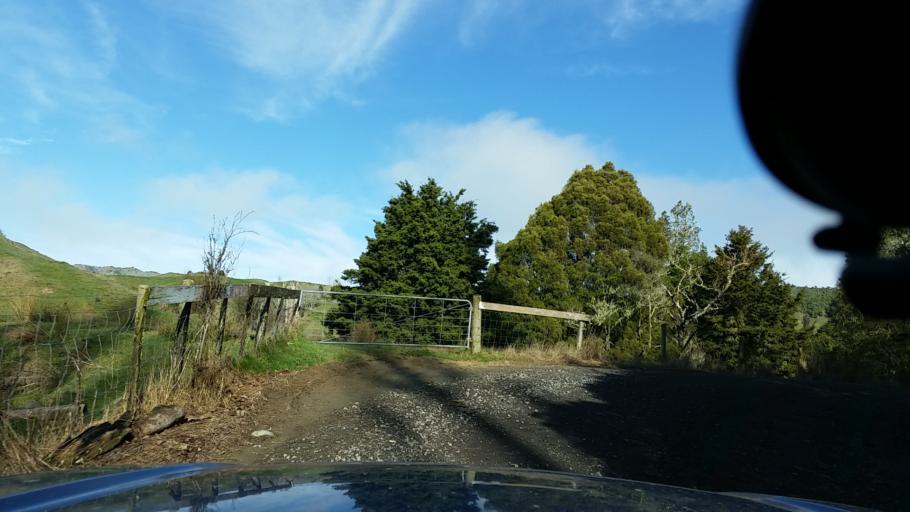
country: NZ
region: Taranaki
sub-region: New Plymouth District
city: Waitara
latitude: -39.0331
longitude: 174.7854
